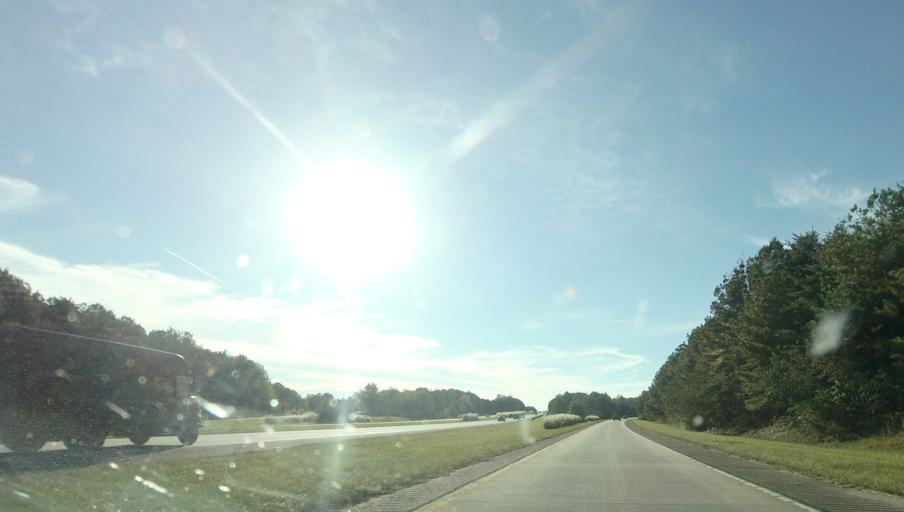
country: US
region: Georgia
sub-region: Muscogee County
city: Columbus
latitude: 32.5544
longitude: -84.9206
